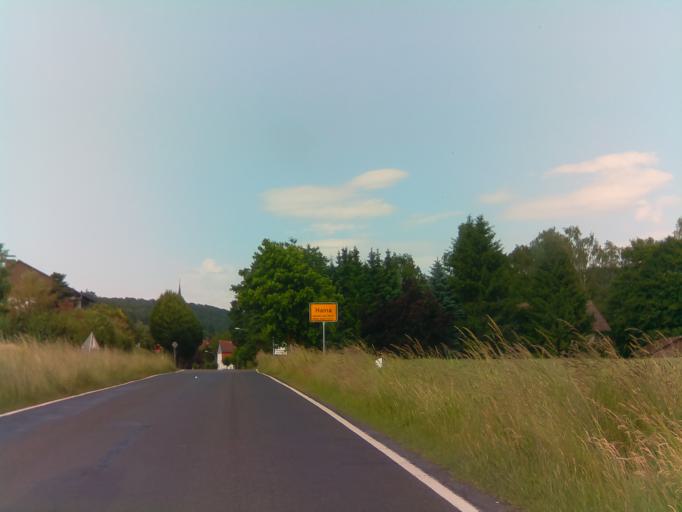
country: DE
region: Hesse
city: Haina
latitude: 51.0232
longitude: 8.9682
